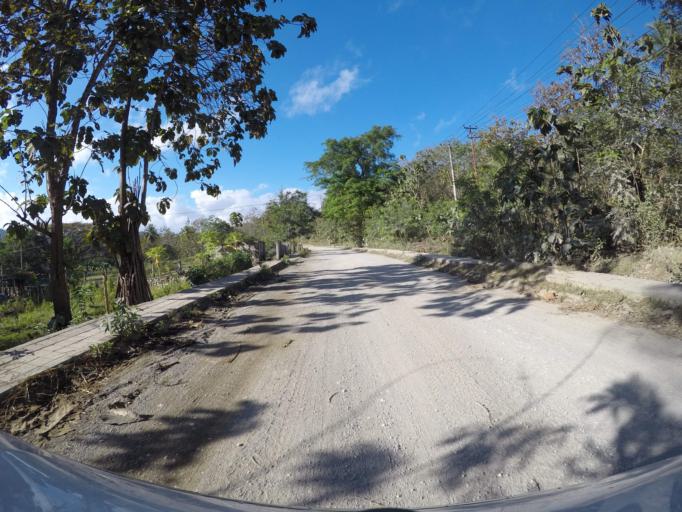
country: TL
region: Viqueque
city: Viqueque
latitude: -8.8432
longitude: 126.3694
